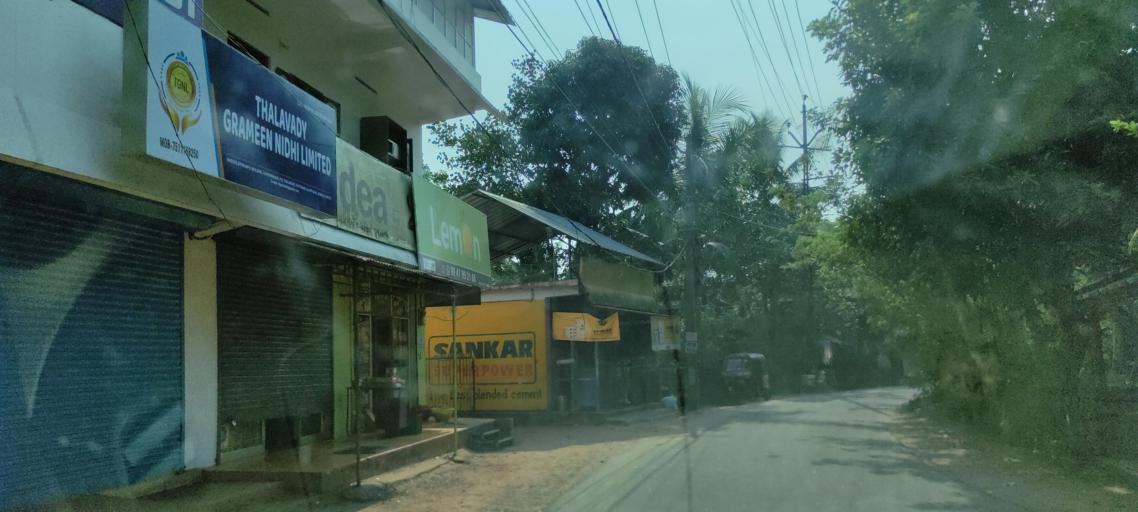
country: IN
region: Kerala
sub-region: Pattanamtitta
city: Tiruvalla
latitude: 9.3604
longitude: 76.4935
